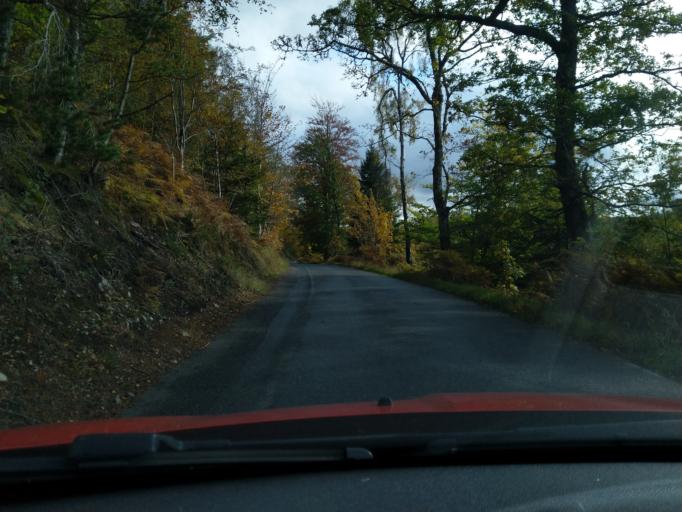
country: GB
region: Scotland
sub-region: Perth and Kinross
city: Aberfeldy
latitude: 56.7077
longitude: -4.0771
